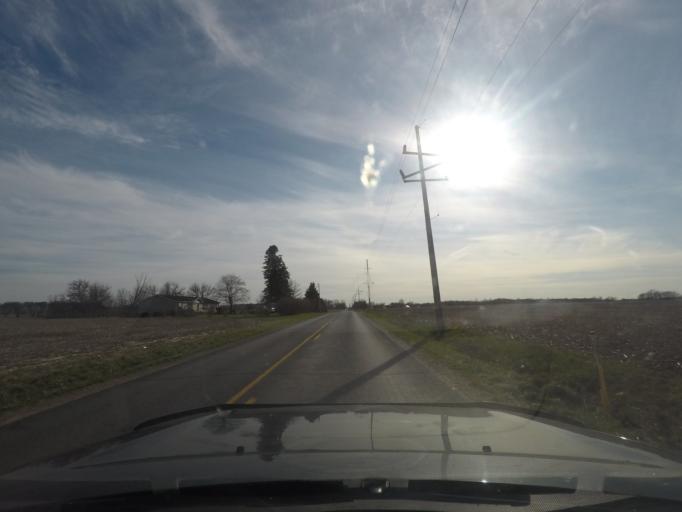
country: US
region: Indiana
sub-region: Elkhart County
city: Wakarusa
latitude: 41.4833
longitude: -86.0413
